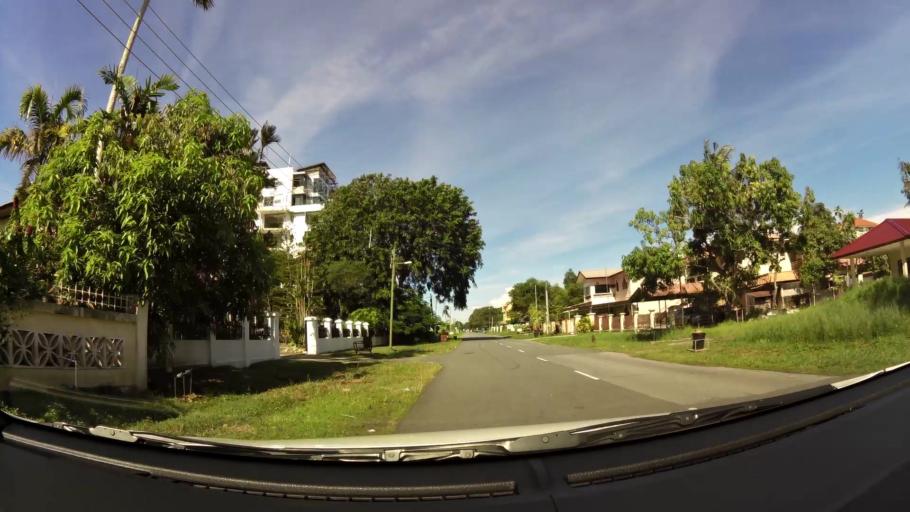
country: BN
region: Belait
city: Kuala Belait
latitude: 4.5833
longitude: 114.2095
